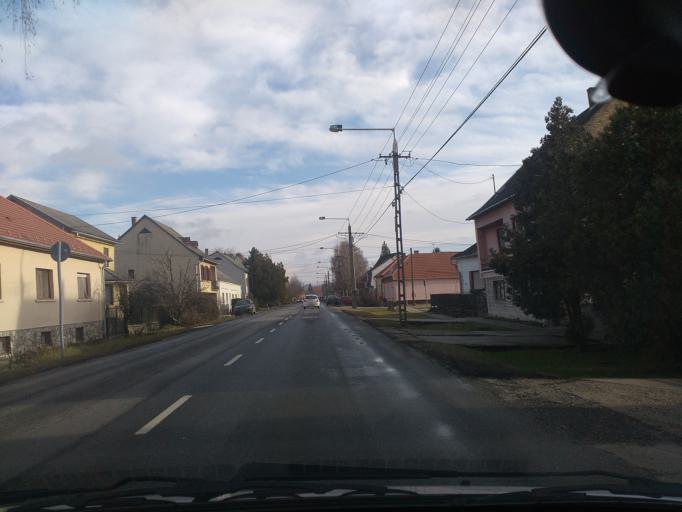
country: HU
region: Komarom-Esztergom
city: Tat
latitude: 47.7484
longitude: 18.6343
